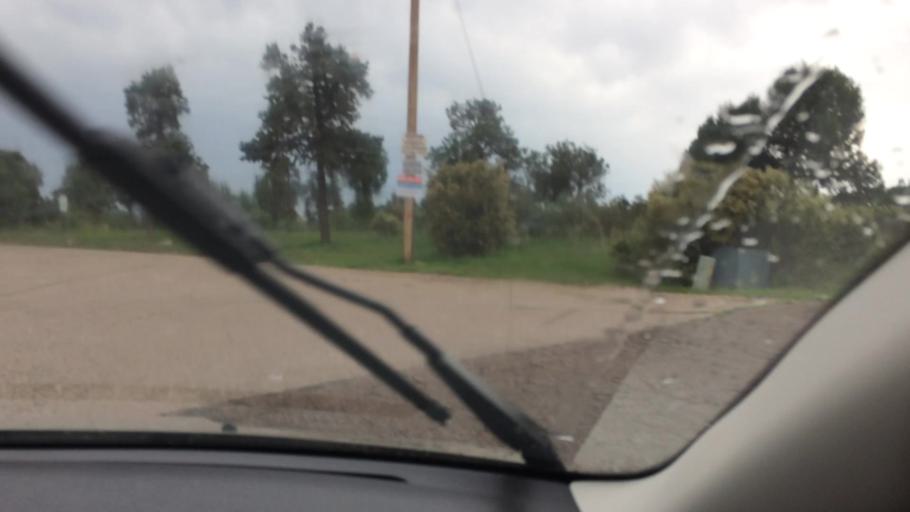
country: US
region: Arizona
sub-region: Navajo County
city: Heber-Overgaard
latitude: 34.4389
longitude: -110.6220
